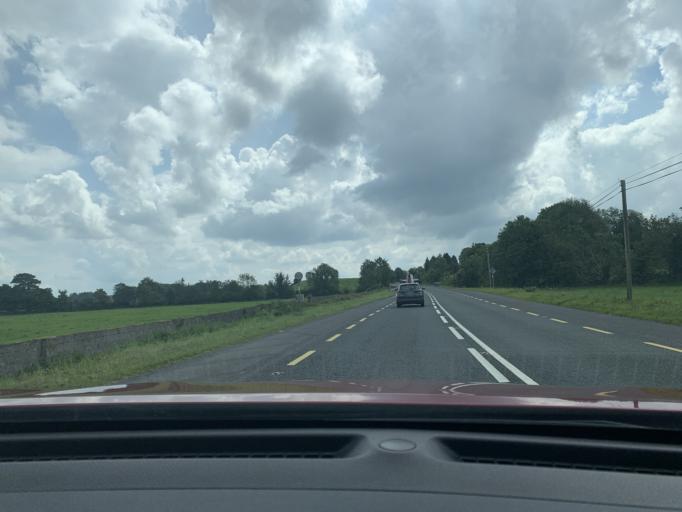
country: IE
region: Connaught
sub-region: Sligo
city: Tobercurry
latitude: 53.9369
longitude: -8.7887
